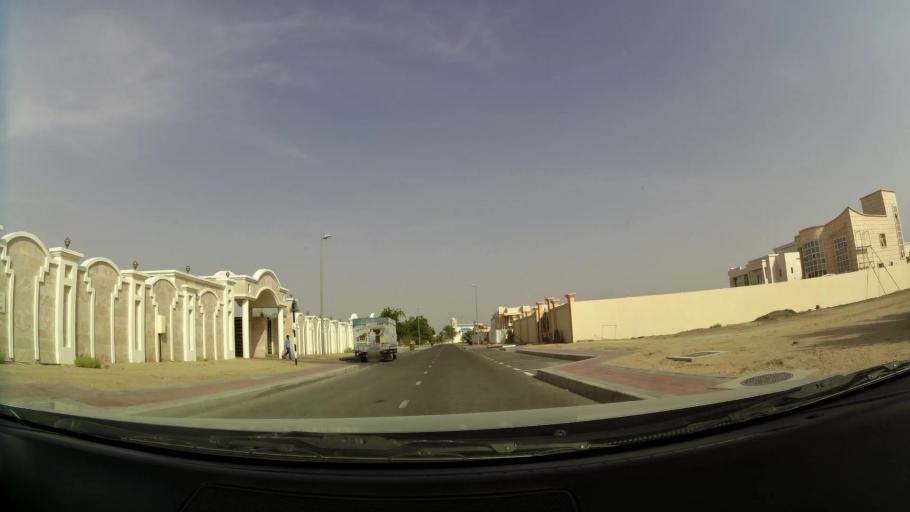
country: AE
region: Abu Dhabi
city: Al Ain
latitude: 24.1338
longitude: 55.7056
